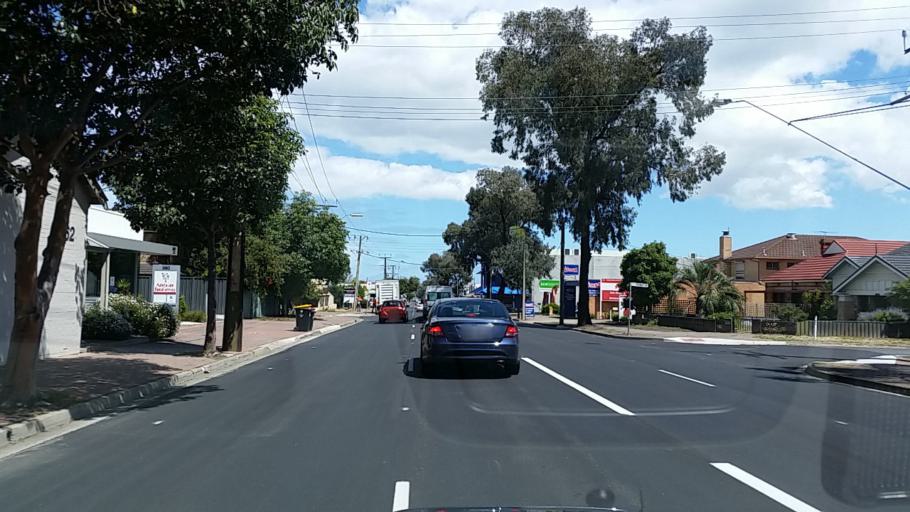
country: AU
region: South Australia
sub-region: Norwood Payneham St Peters
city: Trinity Gardens
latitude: -34.9141
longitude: 138.6547
